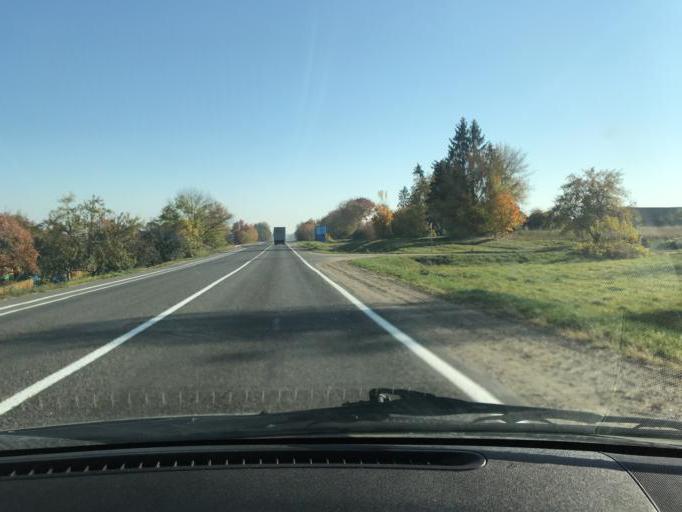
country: BY
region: Minsk
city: Klyetsk
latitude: 52.9704
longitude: 26.6519
